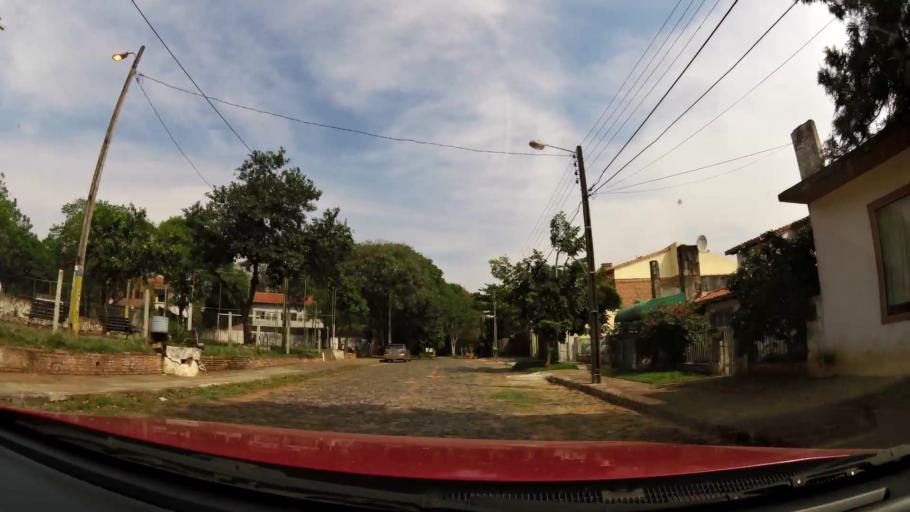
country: PY
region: Asuncion
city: Asuncion
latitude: -25.2630
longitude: -57.5668
